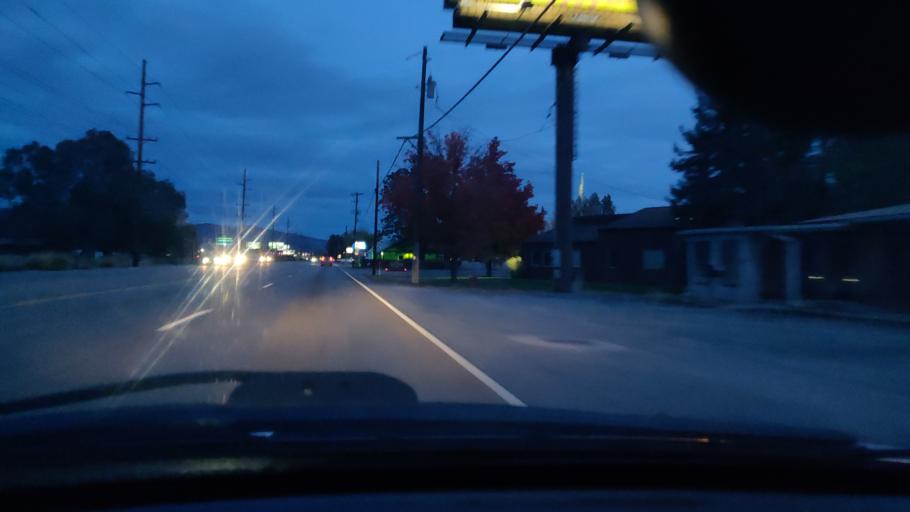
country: US
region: Idaho
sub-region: Ada County
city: Eagle
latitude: 43.6743
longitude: -116.2914
